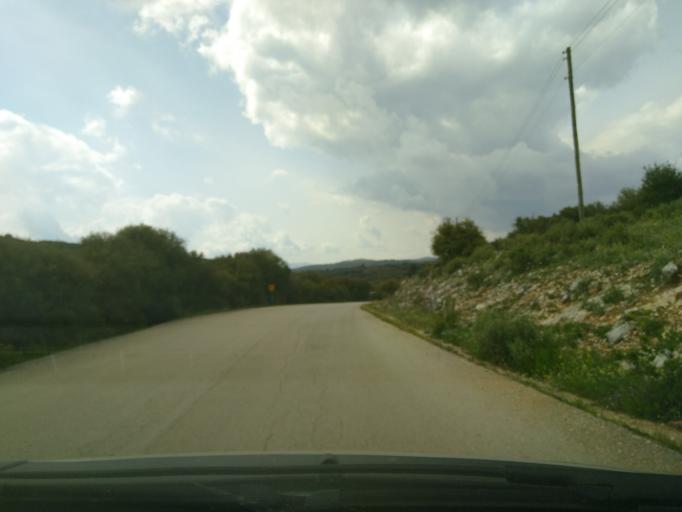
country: GR
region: Epirus
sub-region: Nomos Ioanninon
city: Asprangeloi
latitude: 39.7728
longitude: 20.6922
